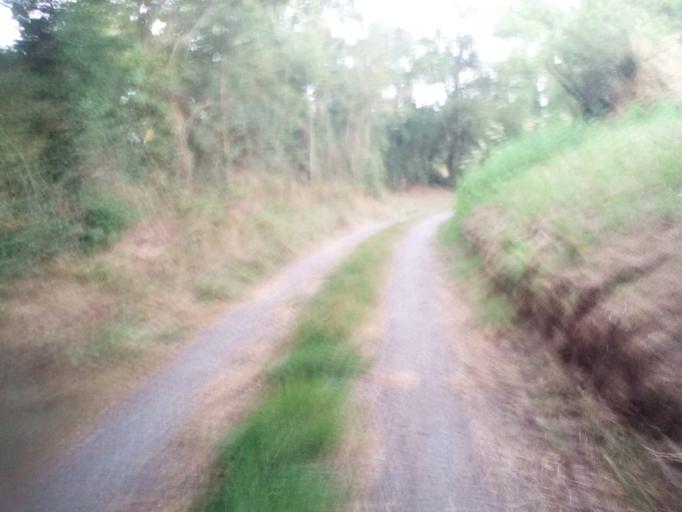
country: FR
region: Lower Normandy
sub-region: Departement du Calvados
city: Bavent
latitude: 49.2350
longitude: -0.1528
